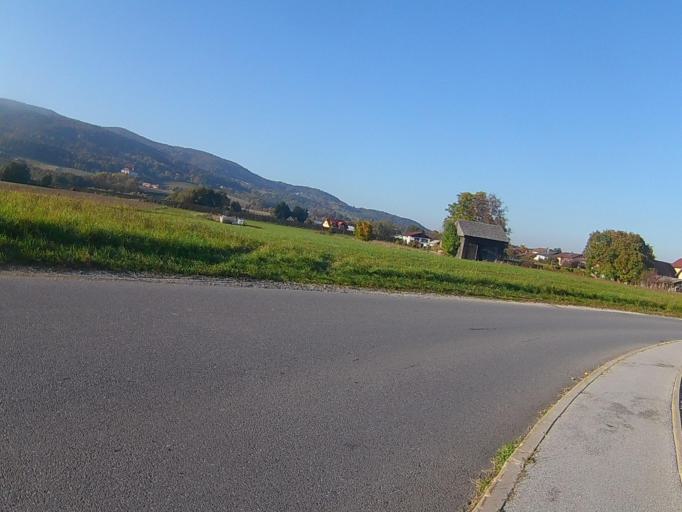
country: SI
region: Hoce-Slivnica
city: Spodnje Hoce
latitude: 46.4945
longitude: 15.6351
